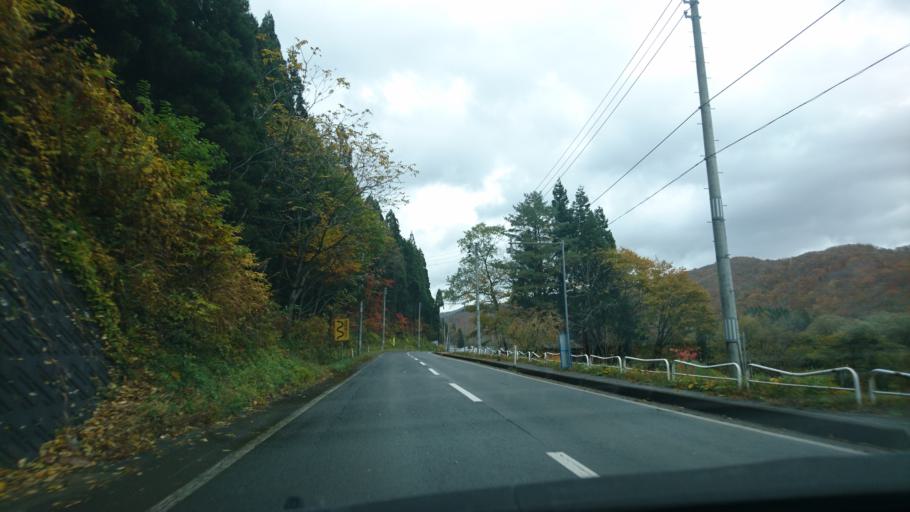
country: JP
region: Iwate
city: Shizukuishi
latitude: 39.5030
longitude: 140.8201
